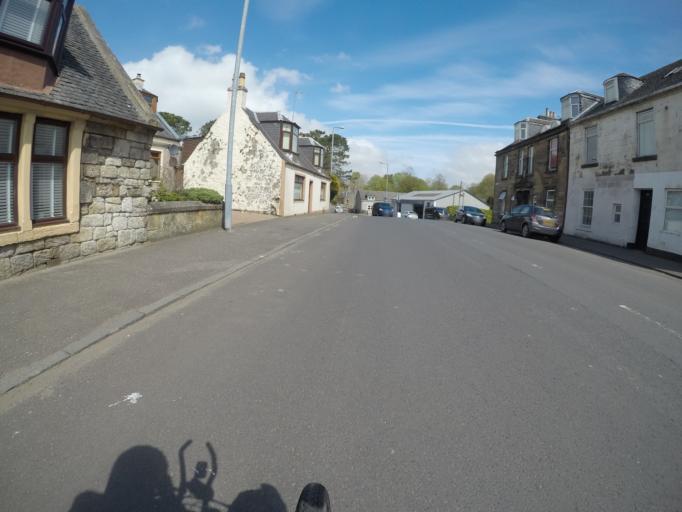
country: GB
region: Scotland
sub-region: East Ayrshire
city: Stewarton
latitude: 55.6827
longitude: -4.5105
